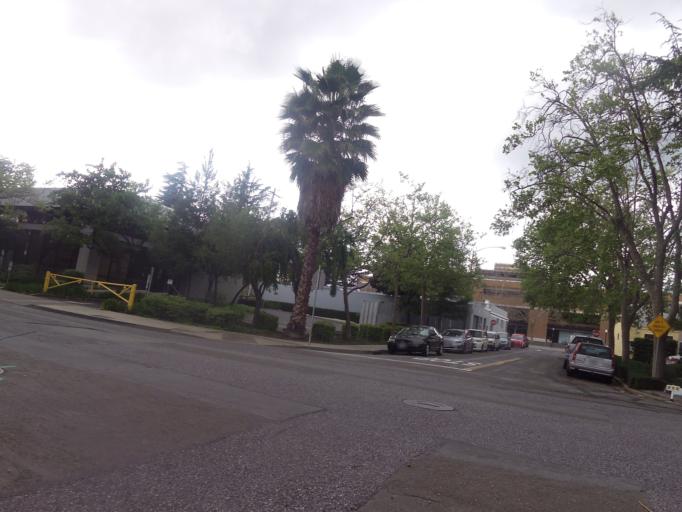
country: US
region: California
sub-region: Santa Clara County
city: Mountain View
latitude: 37.3860
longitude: -122.0826
